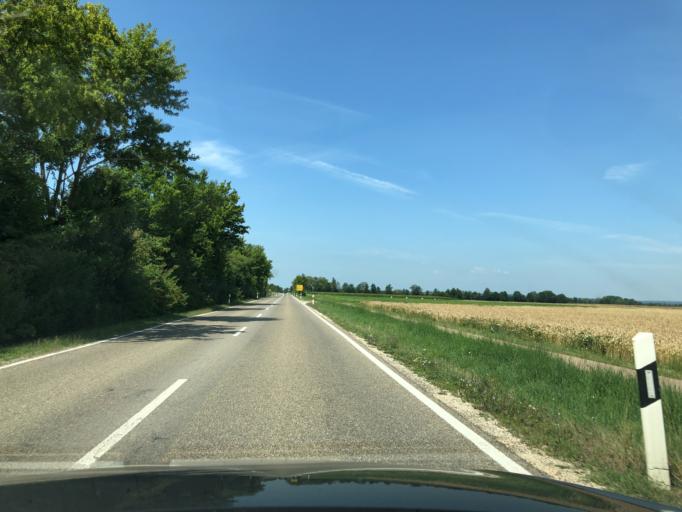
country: DE
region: Bavaria
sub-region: Swabia
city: Oberndorf
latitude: 48.6649
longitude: 10.8578
